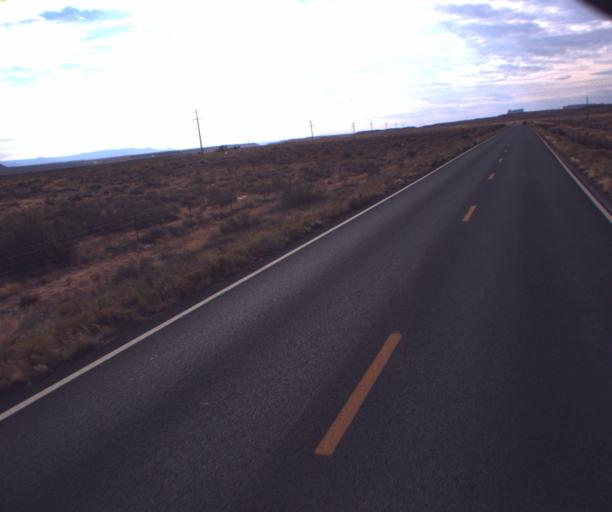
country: US
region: Arizona
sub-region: Apache County
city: Many Farms
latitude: 36.6230
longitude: -109.5824
